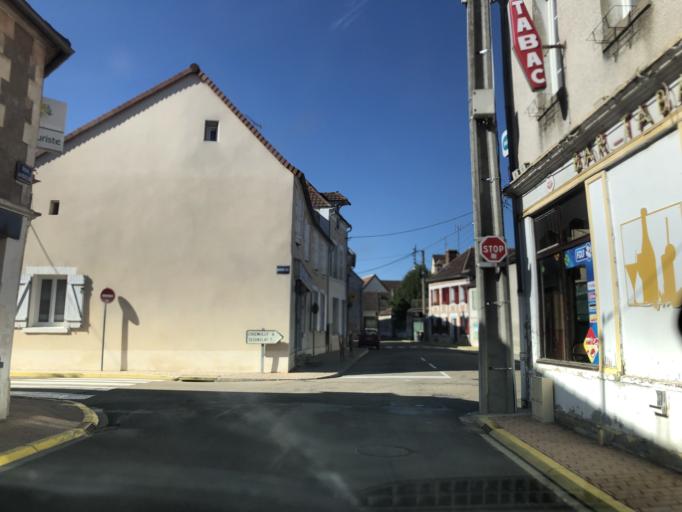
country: FR
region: Bourgogne
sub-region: Departement de l'Yonne
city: Appoigny
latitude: 47.8755
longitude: 3.5265
